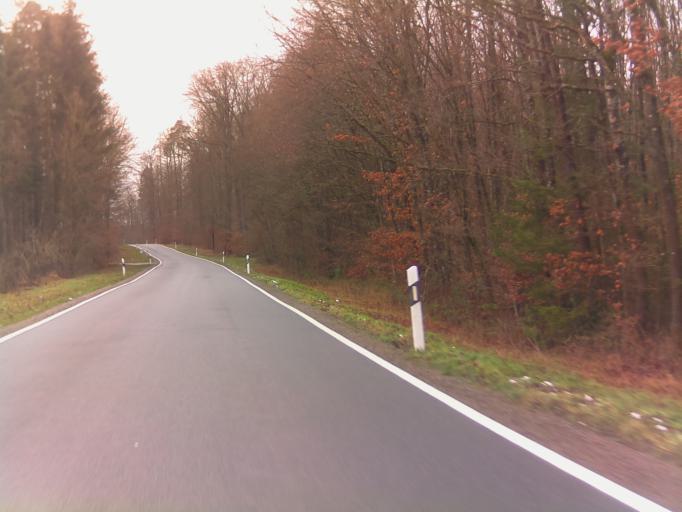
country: DE
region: Bavaria
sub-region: Regierungsbezirk Unterfranken
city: Schonau
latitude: 50.0816
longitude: 9.7582
